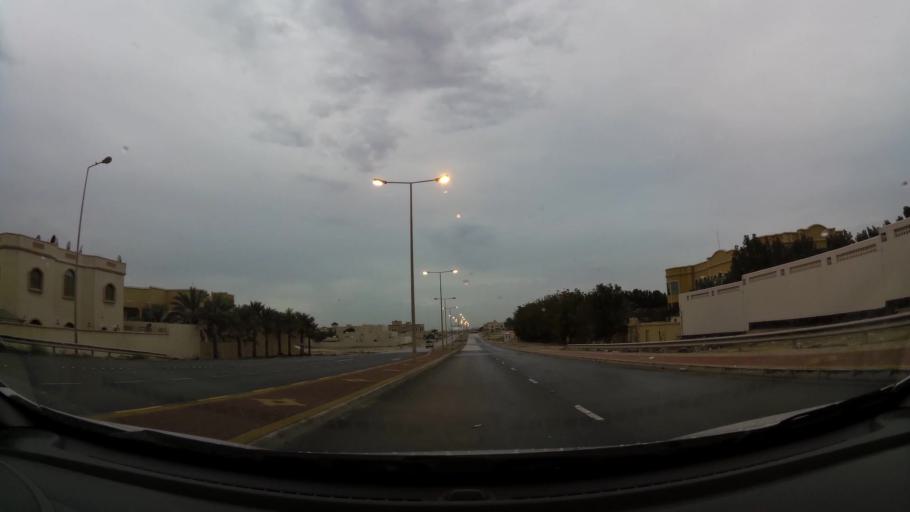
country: BH
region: Central Governorate
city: Madinat Hamad
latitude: 26.1418
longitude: 50.5171
